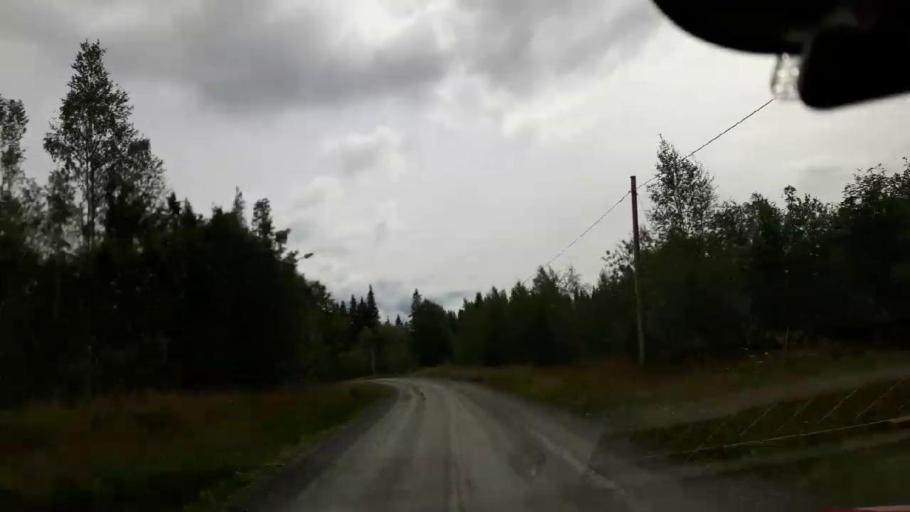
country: SE
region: Jaemtland
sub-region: Krokoms Kommun
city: Valla
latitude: 63.6724
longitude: 13.9506
